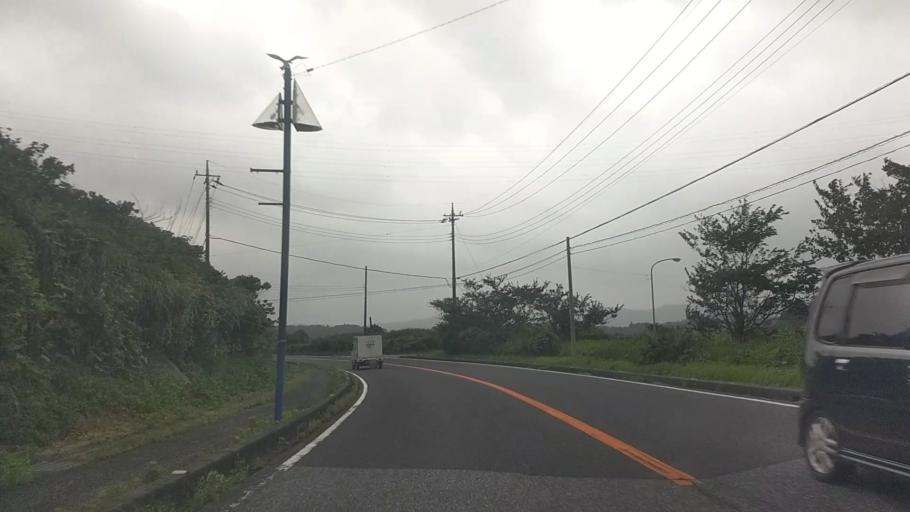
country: JP
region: Chiba
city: Kawaguchi
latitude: 35.1417
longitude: 140.0689
